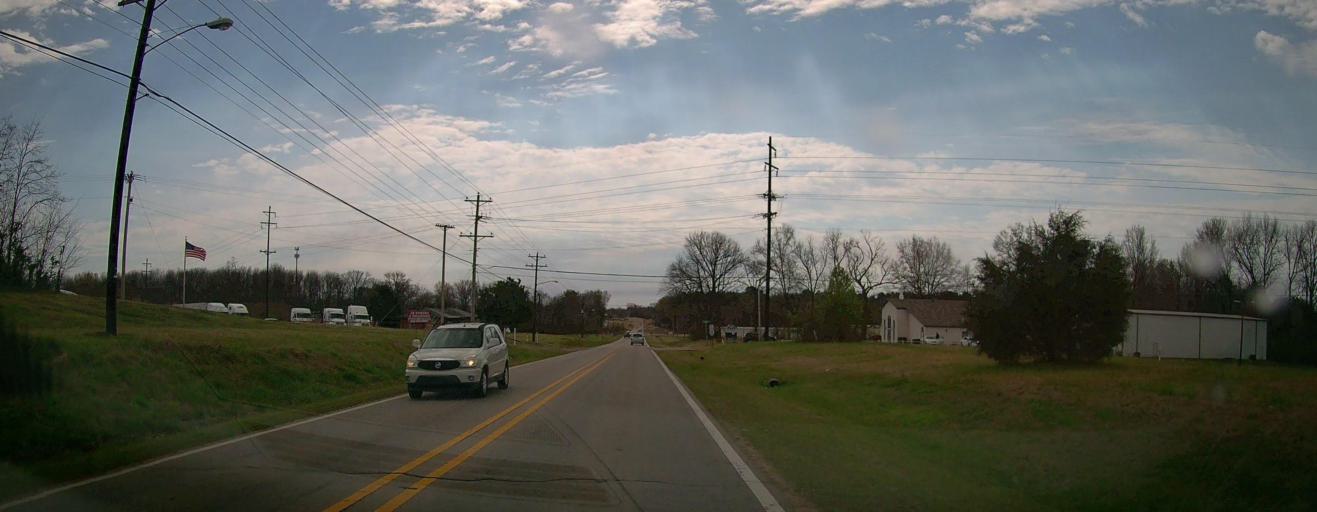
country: US
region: Mississippi
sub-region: De Soto County
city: Olive Branch
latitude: 34.9484
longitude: -89.8109
